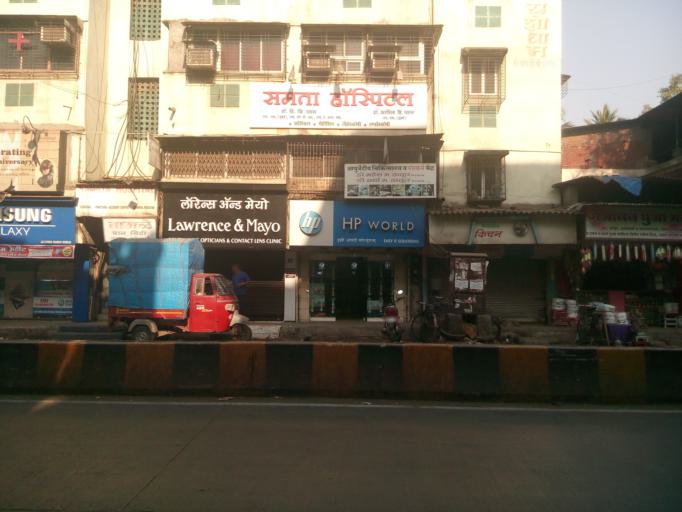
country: IN
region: Maharashtra
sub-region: Thane
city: Dombivli
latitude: 19.2140
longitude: 73.0911
